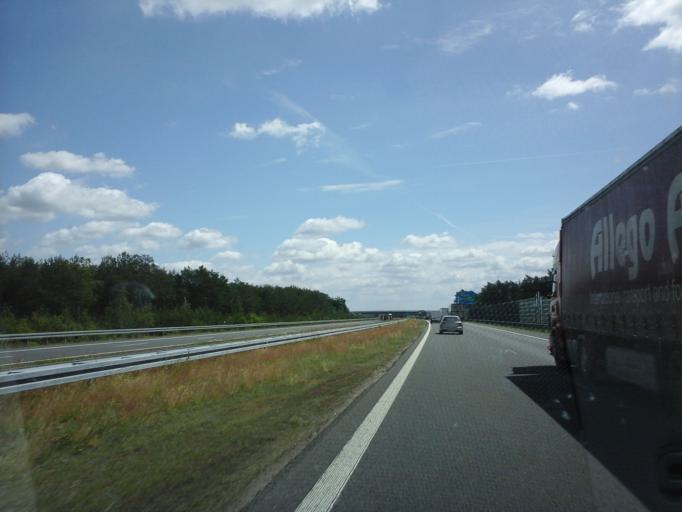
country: PL
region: Greater Poland Voivodeship
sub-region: Powiat kolski
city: Dabie
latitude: 52.0785
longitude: 18.8011
